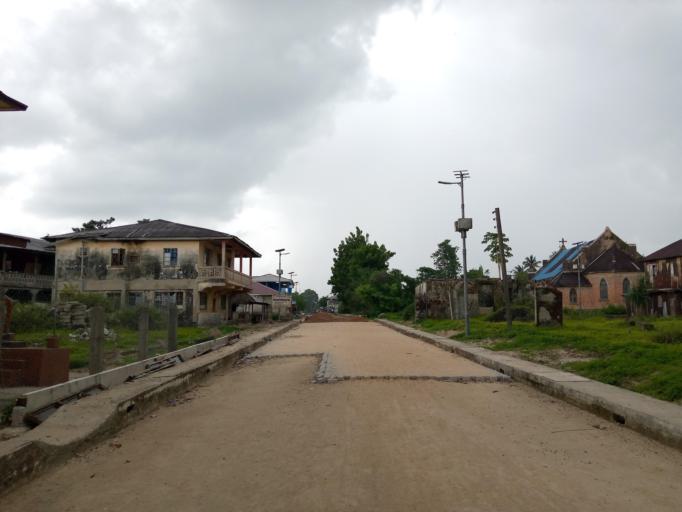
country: SL
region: Southern Province
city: Bonthe
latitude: 7.5306
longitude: -12.5023
